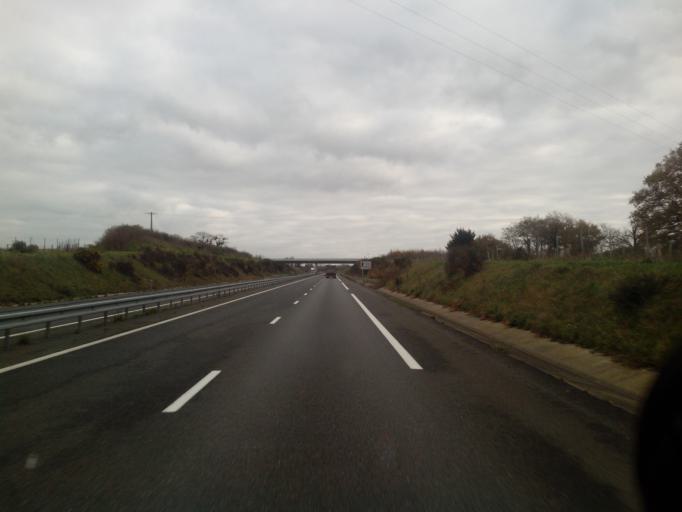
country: FR
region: Poitou-Charentes
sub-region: Departement des Deux-Sevres
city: Saint-Pierre-des-Echaubrognes
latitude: 46.9568
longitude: -0.7793
